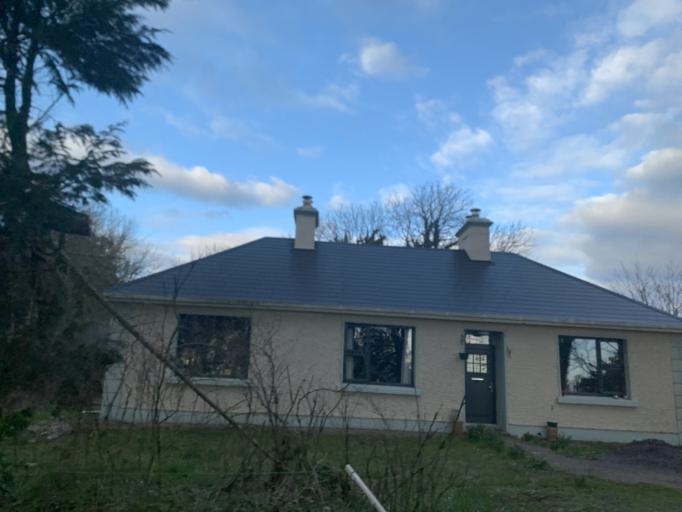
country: IE
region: Connaught
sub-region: Maigh Eo
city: Ballyhaunis
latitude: 53.8576
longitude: -8.7381
